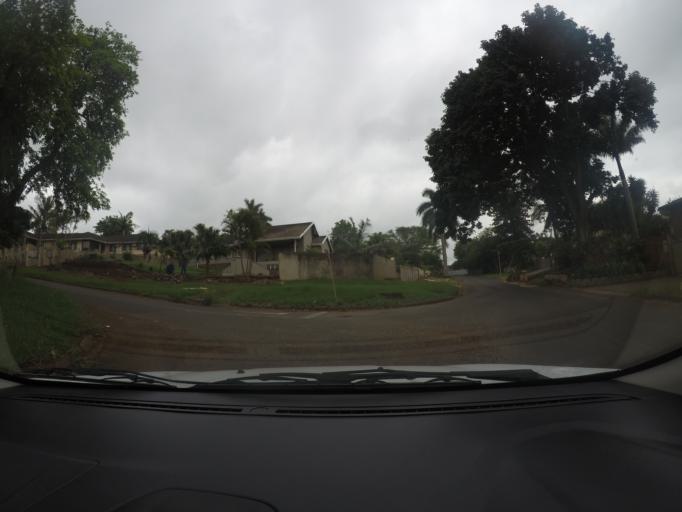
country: ZA
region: KwaZulu-Natal
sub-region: uThungulu District Municipality
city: Empangeni
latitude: -28.7655
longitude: 31.8946
